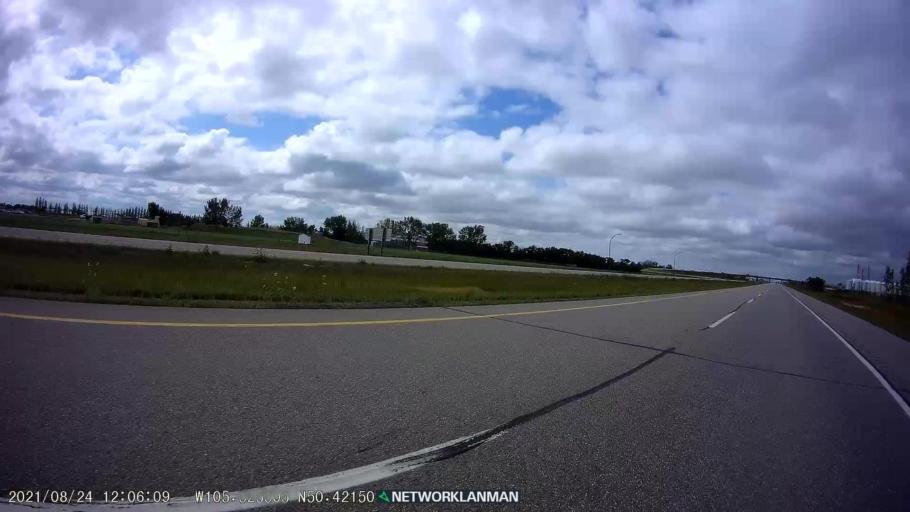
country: CA
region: Saskatchewan
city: Moose Jaw
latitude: 50.4230
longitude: -105.5251
